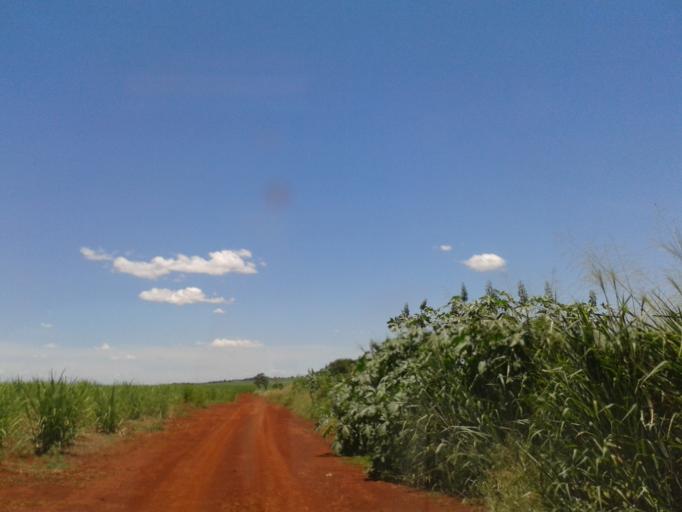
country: BR
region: Minas Gerais
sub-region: Centralina
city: Centralina
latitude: -18.6706
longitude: -49.2414
